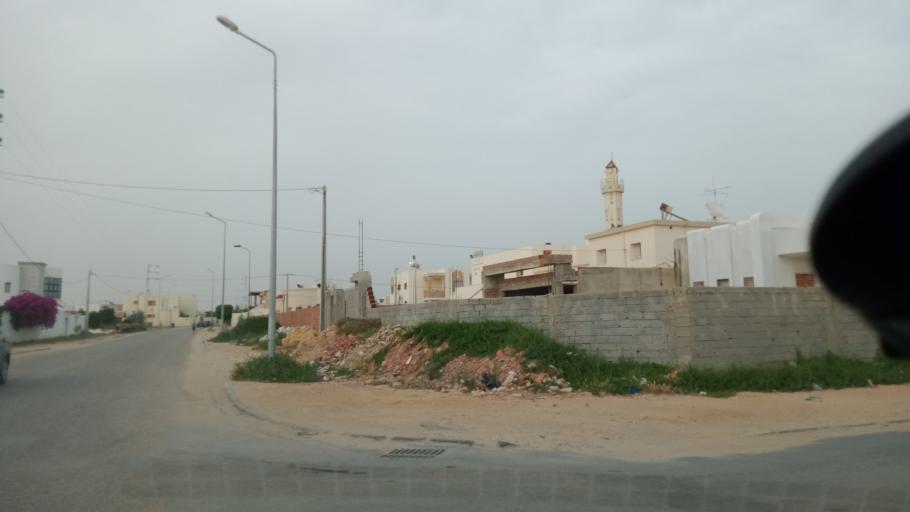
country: TN
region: Safaqis
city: Al Qarmadah
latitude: 34.7909
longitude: 10.7712
